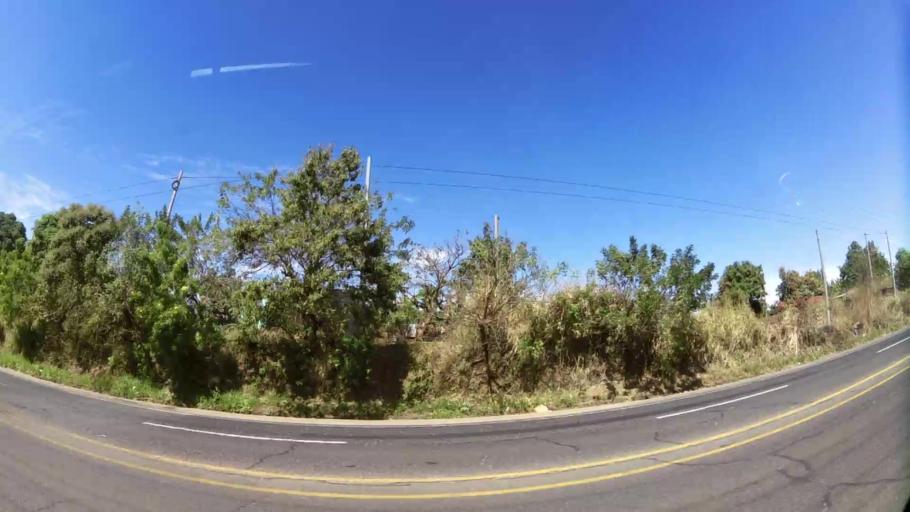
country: SV
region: Santa Ana
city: Chalchuapa
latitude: 13.9735
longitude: -89.6965
